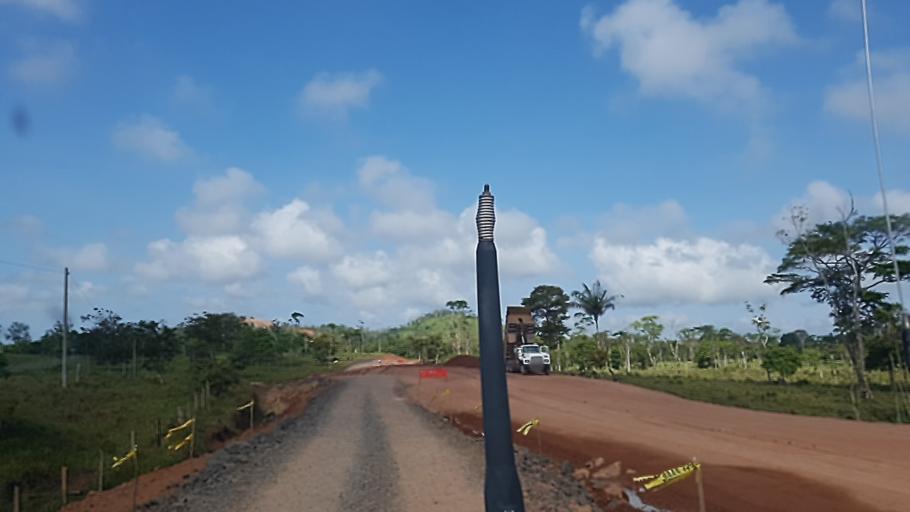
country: NI
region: Atlantico Sur
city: Bluefields
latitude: 11.8455
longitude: -84.0546
